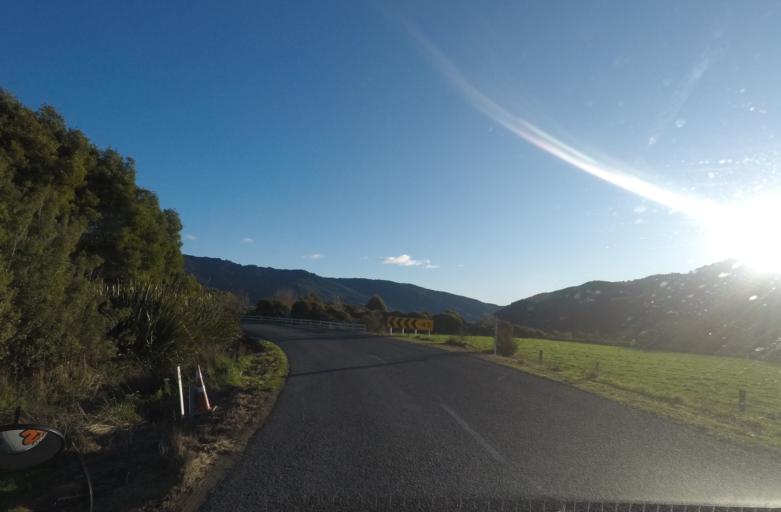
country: NZ
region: Marlborough
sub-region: Marlborough District
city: Picton
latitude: -41.2892
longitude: 173.8480
